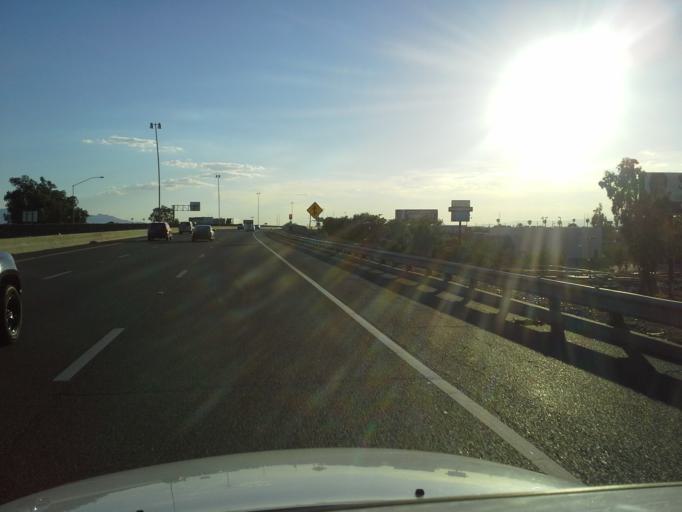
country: US
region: Arizona
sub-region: Maricopa County
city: Phoenix
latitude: 33.4288
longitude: -112.0665
